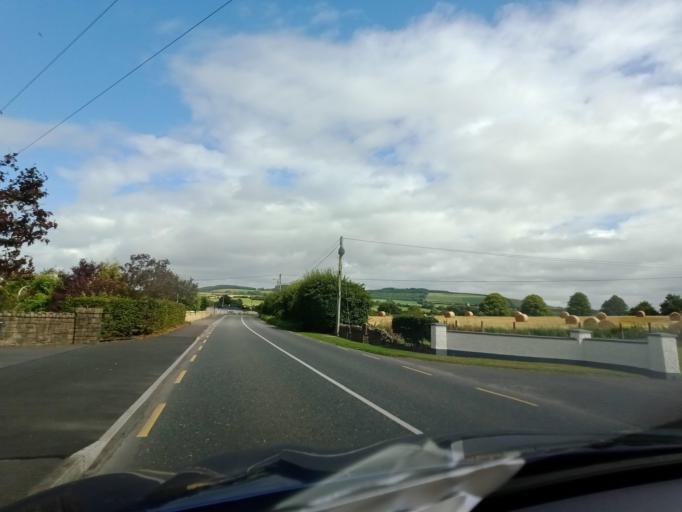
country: IE
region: Leinster
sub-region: Laois
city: Abbeyleix
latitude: 52.9457
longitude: -7.3123
